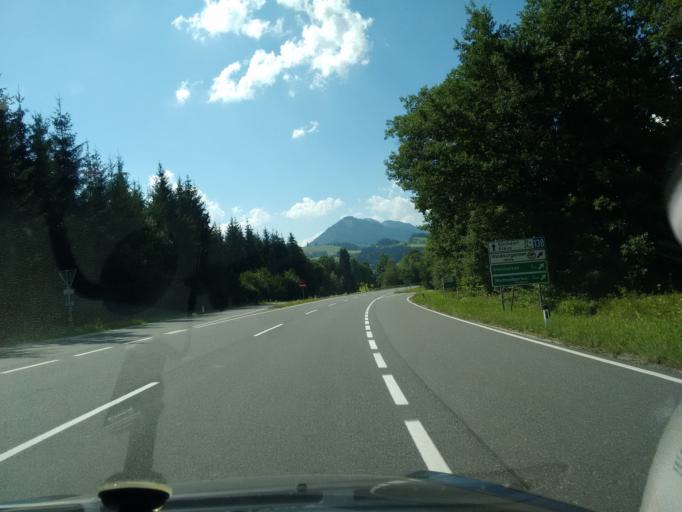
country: AT
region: Upper Austria
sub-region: Politischer Bezirk Kirchdorf an der Krems
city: Rossleithen
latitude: 47.7138
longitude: 14.3180
